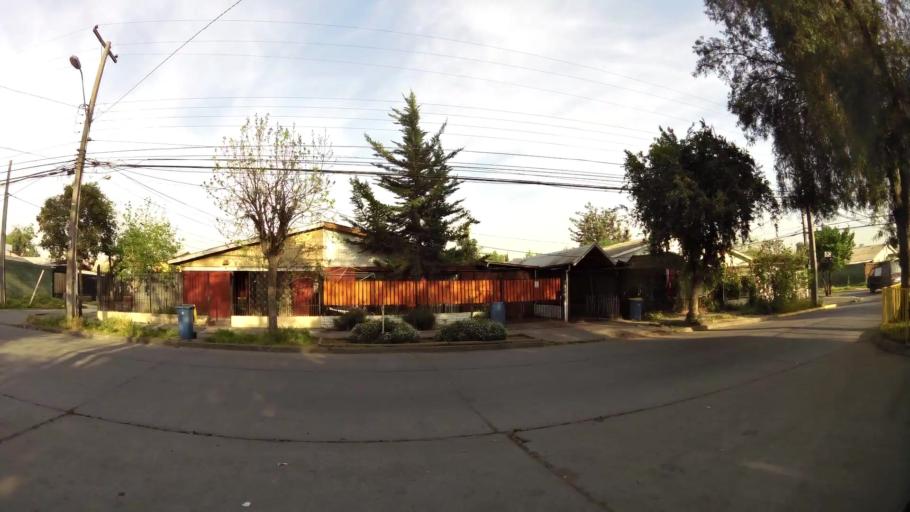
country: CL
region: Santiago Metropolitan
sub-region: Provincia de Santiago
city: Villa Presidente Frei, Nunoa, Santiago, Chile
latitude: -33.5187
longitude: -70.5853
